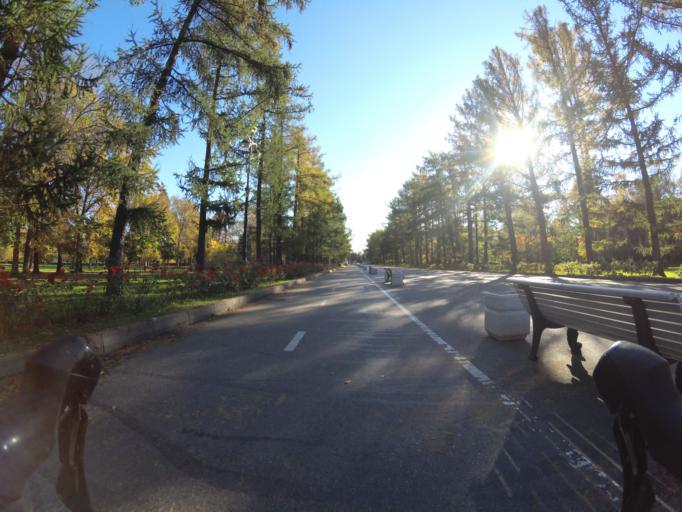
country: RU
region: Leningrad
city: Krestovskiy ostrov
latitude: 59.9711
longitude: 30.2435
